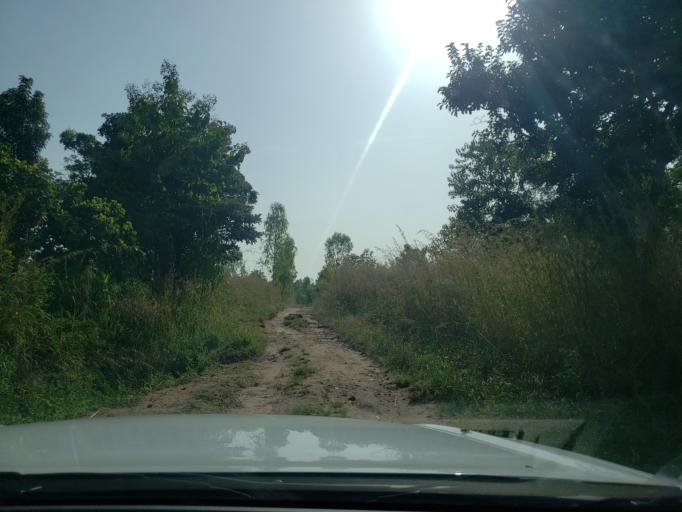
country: TG
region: Kara
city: Bafilo
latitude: 9.4105
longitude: 1.1777
